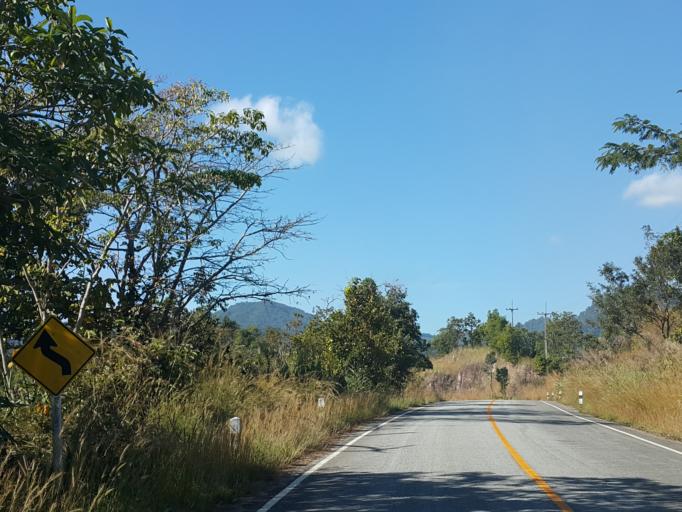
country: TH
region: Chiang Mai
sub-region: Amphoe Chiang Dao
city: Chiang Dao
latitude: 19.5264
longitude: 98.8698
